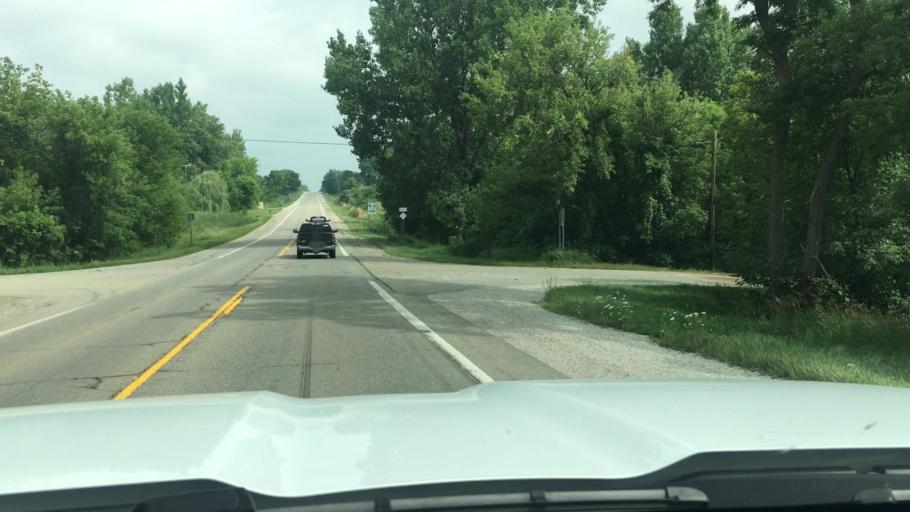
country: US
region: Michigan
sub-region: Lapeer County
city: Imlay City
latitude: 43.1091
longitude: -83.0723
